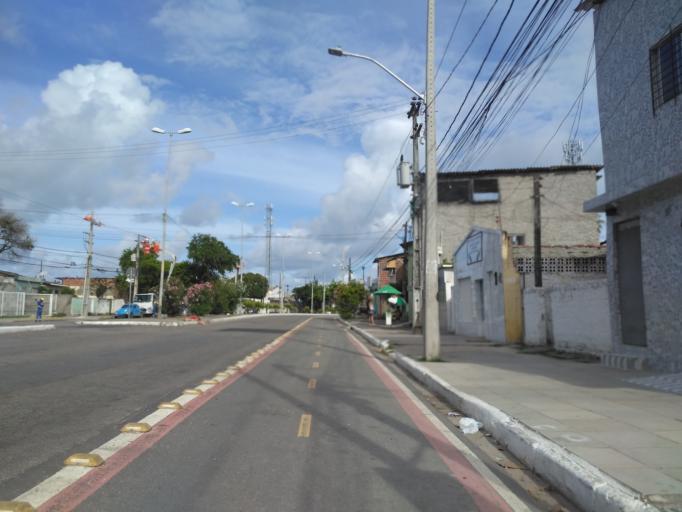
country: BR
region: Pernambuco
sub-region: Recife
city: Recife
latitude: -8.0426
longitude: -34.8769
